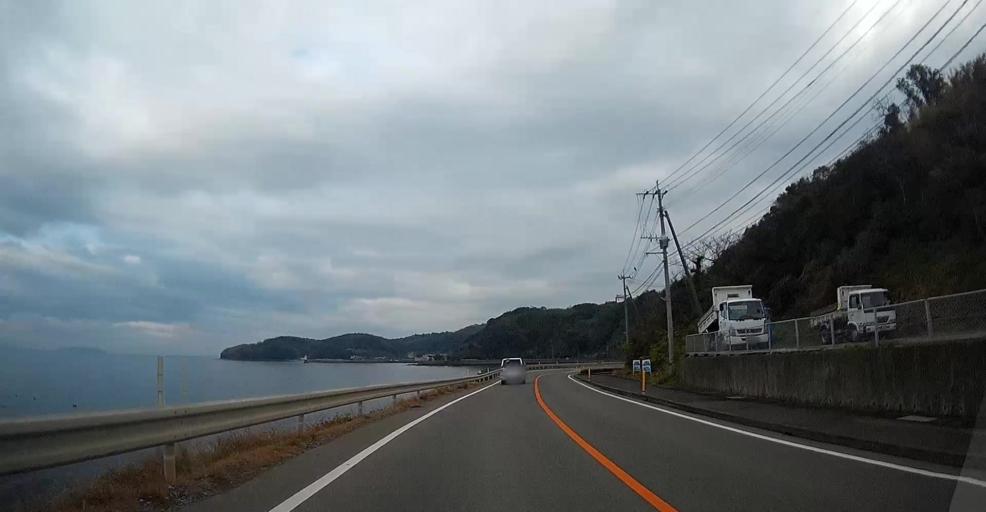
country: JP
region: Kumamoto
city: Hondo
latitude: 32.4869
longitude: 130.2852
